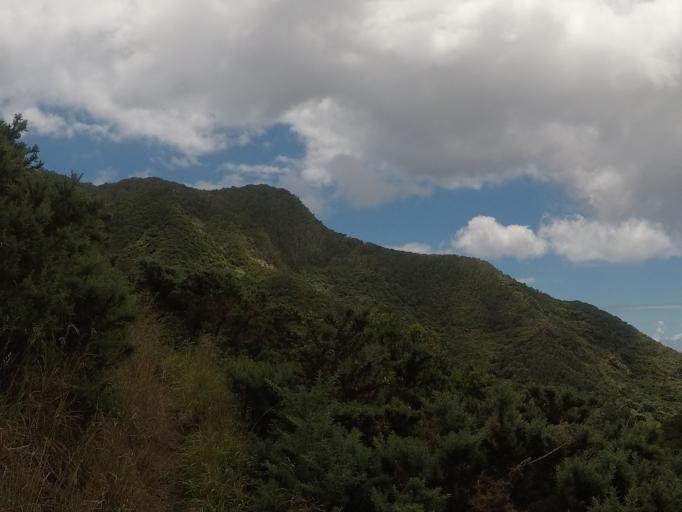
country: PT
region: Madeira
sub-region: Machico
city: Canical
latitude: 32.7551
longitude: -16.7719
